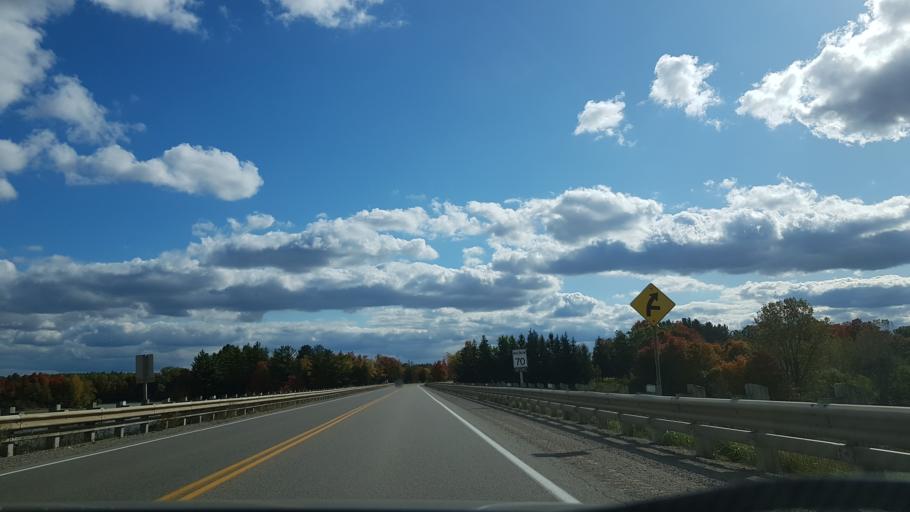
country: CA
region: Ontario
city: South Huron
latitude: 43.1754
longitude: -81.6798
